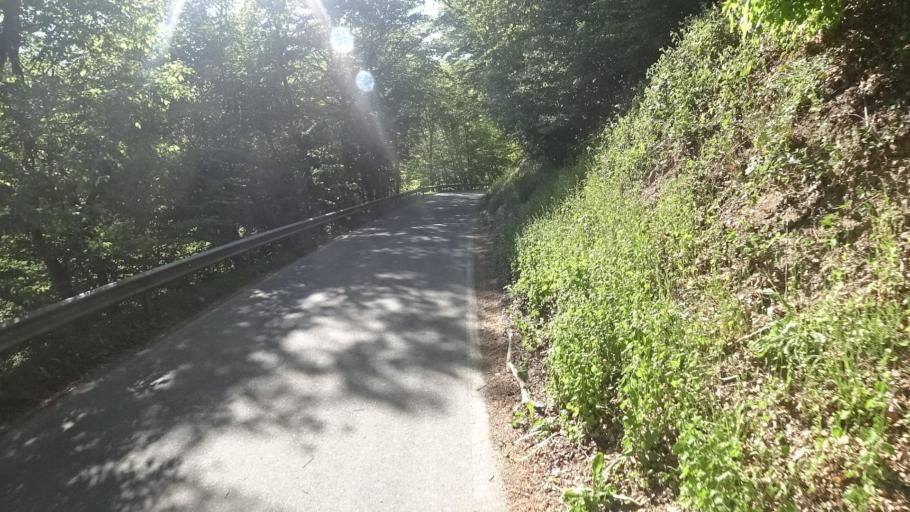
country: DE
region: Rheinland-Pfalz
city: Lind
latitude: 50.4836
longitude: 6.9119
